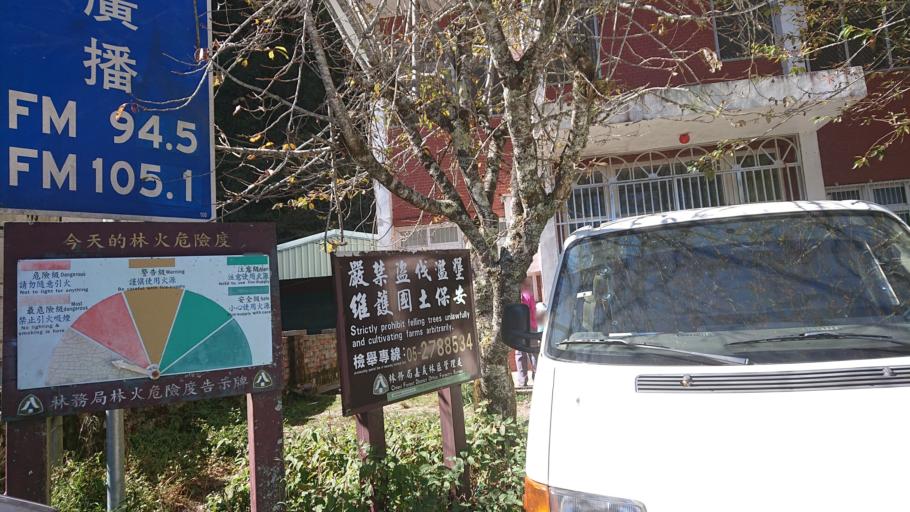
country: TW
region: Taiwan
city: Lugu
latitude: 23.4840
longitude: 120.8303
